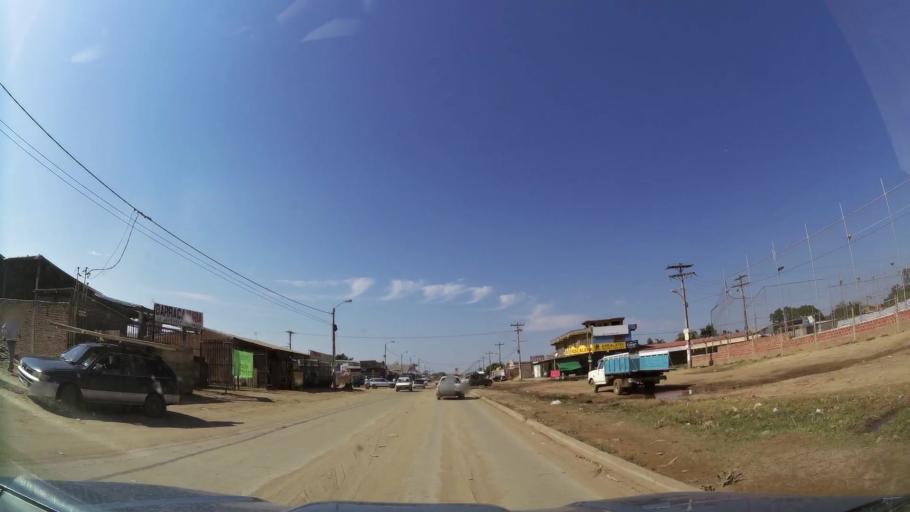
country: BO
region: Santa Cruz
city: Cotoca
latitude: -17.7323
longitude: -63.0967
